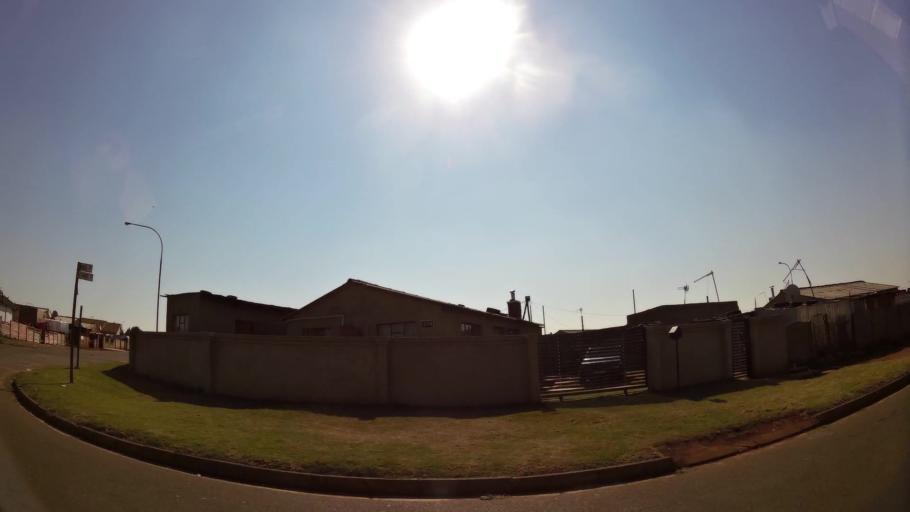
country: ZA
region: Gauteng
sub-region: Ekurhuleni Metropolitan Municipality
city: Benoni
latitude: -26.2263
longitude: 28.3009
